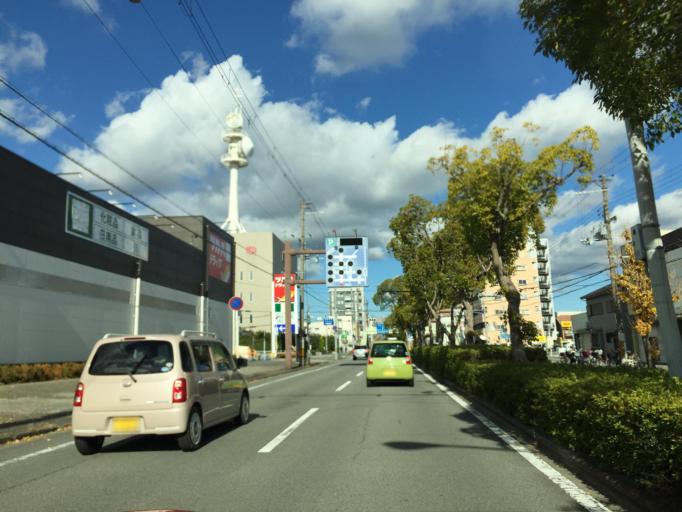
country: JP
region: Wakayama
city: Wakayama-shi
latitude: 34.2246
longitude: 135.1783
